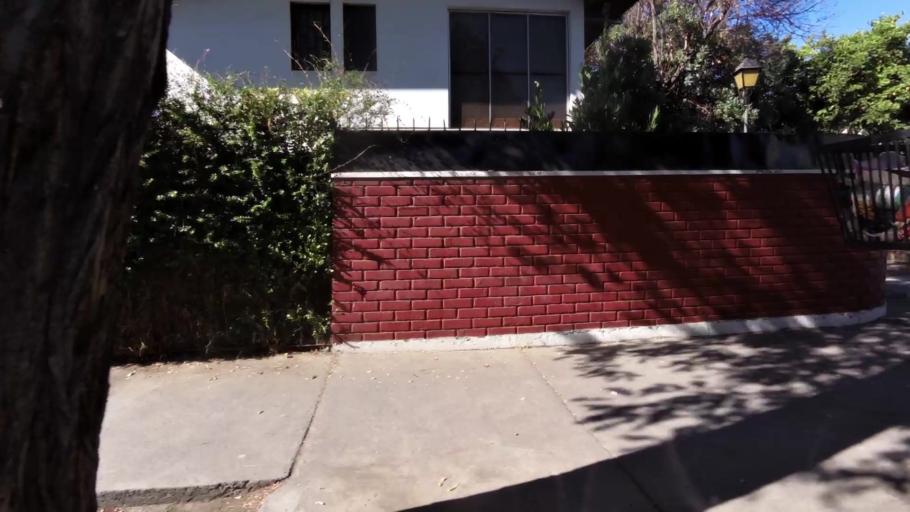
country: CL
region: O'Higgins
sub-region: Provincia de Cachapoal
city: Rancagua
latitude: -34.1683
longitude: -70.7387
